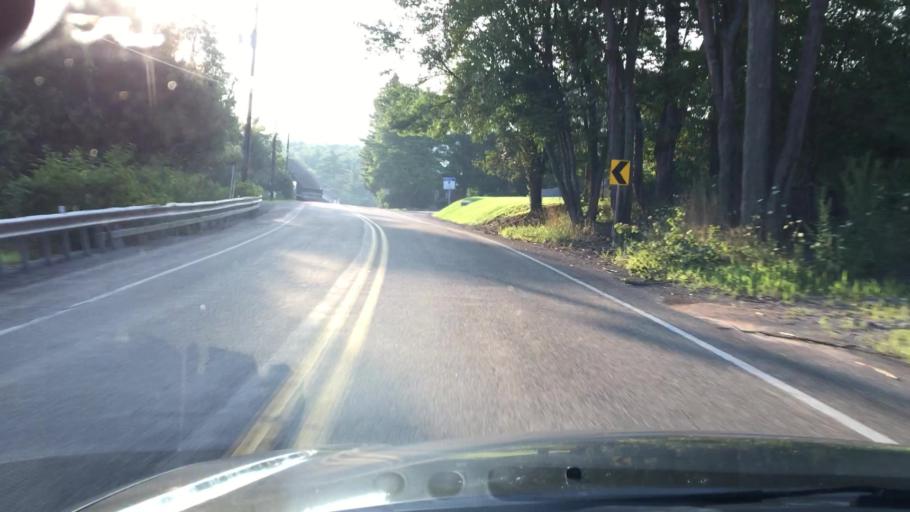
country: US
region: Pennsylvania
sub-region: Carbon County
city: Weatherly
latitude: 40.9149
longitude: -75.8515
